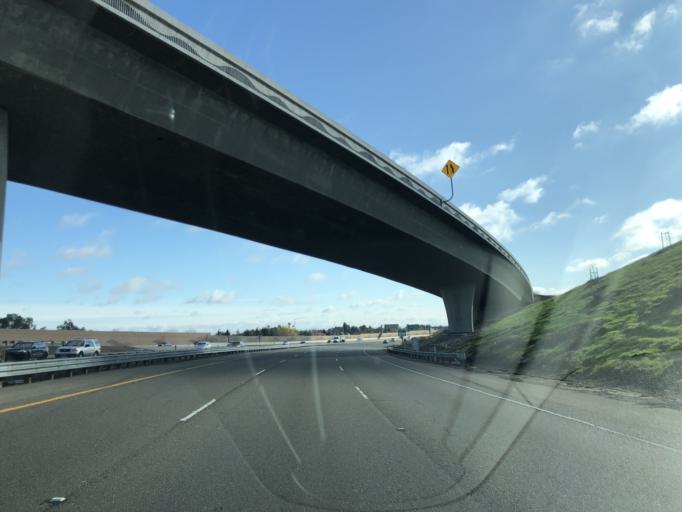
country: US
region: California
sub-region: Contra Costa County
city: Oakley
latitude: 37.9900
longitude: -121.7562
